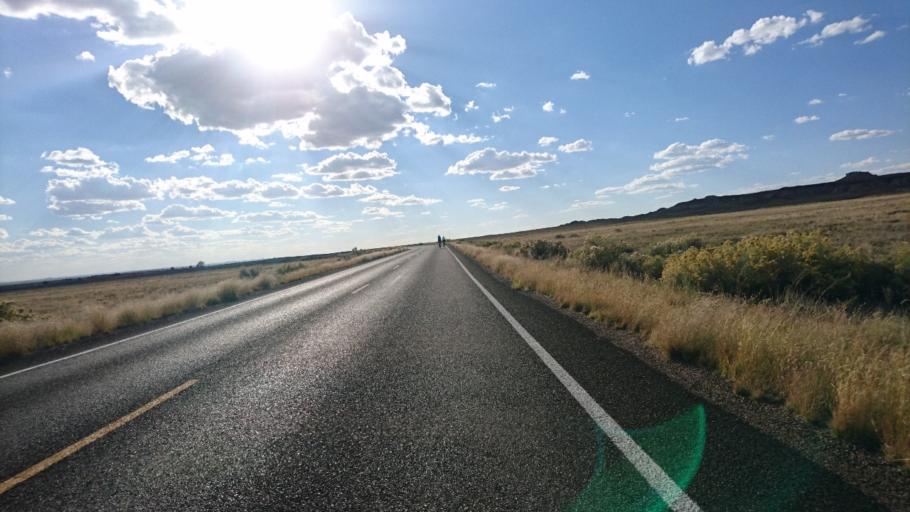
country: US
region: Arizona
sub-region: Navajo County
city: Holbrook
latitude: 34.8030
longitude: -109.8804
